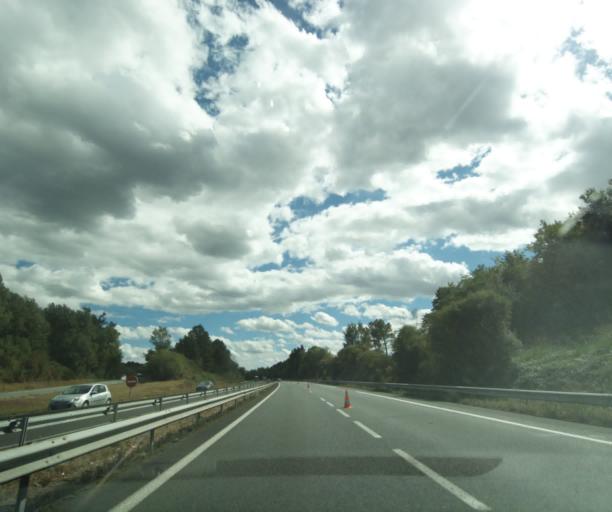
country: FR
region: Aquitaine
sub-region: Departement de la Gironde
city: Gironde-sur-Dropt
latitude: 44.5199
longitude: -0.0833
